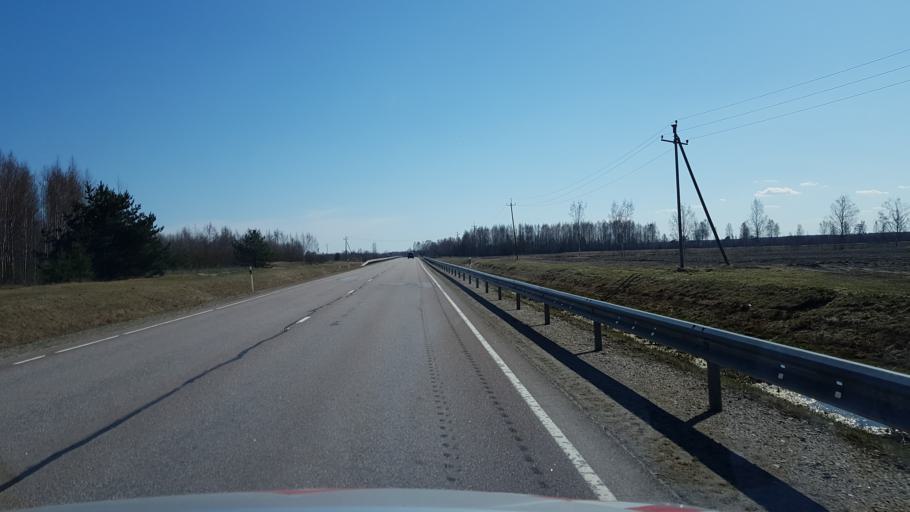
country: EE
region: Jogevamaa
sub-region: Mustvee linn
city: Mustvee
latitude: 58.8167
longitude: 26.9358
